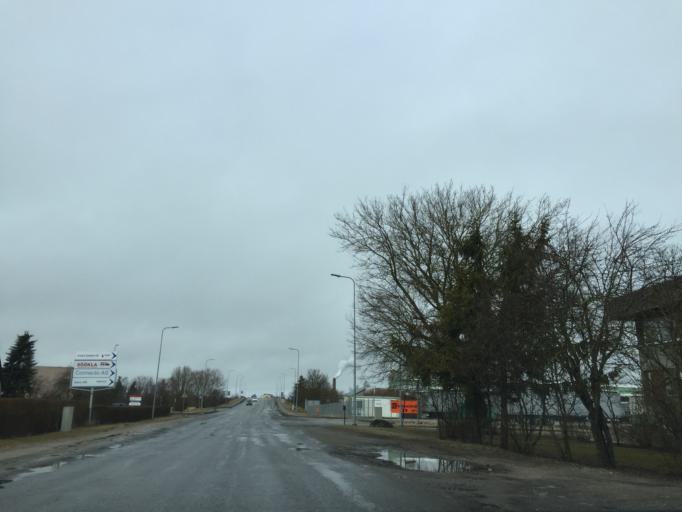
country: EE
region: Laeaene
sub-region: Haapsalu linn
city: Haapsalu
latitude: 58.9275
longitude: 23.5446
